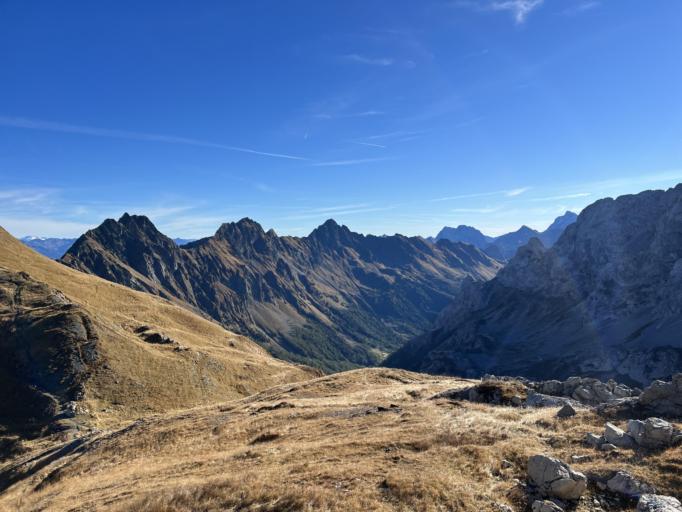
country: IT
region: Friuli Venezia Giulia
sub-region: Provincia di Udine
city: Forni Avoltri
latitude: 46.6321
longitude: 12.7299
